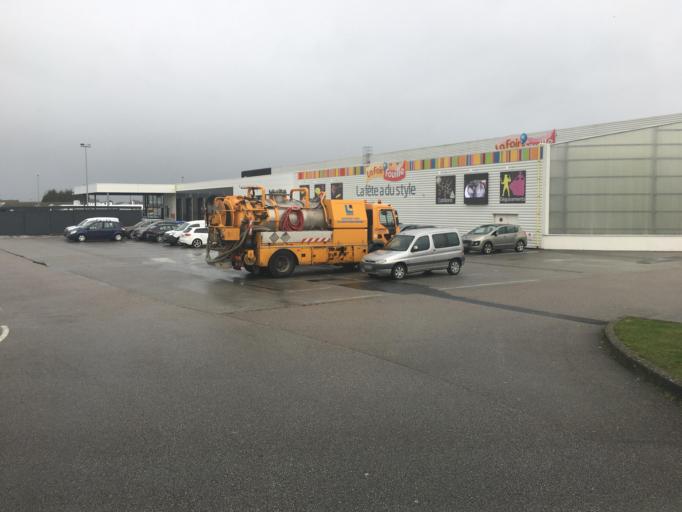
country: FR
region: Lower Normandy
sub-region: Departement de la Manche
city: Cherbourg-Octeville
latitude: 49.6332
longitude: -1.5918
